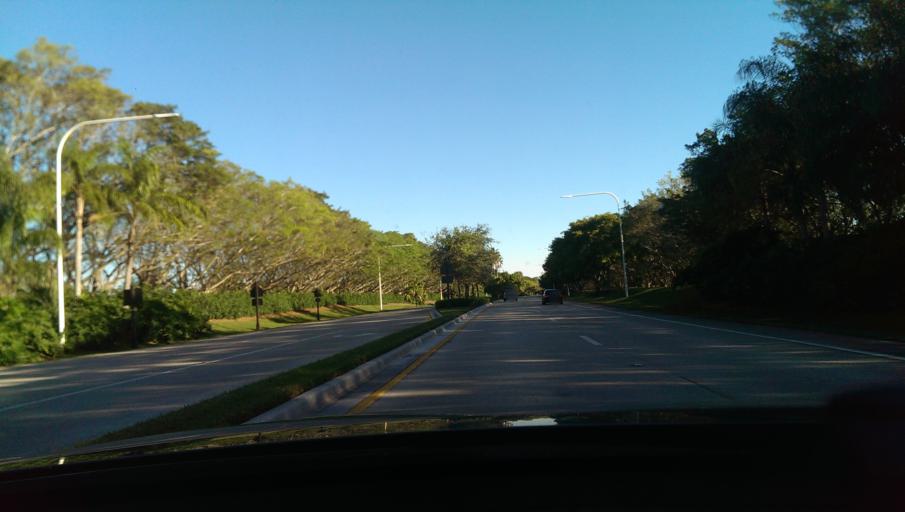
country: US
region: Florida
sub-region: Broward County
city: Weston
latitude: 26.0748
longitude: -80.3931
